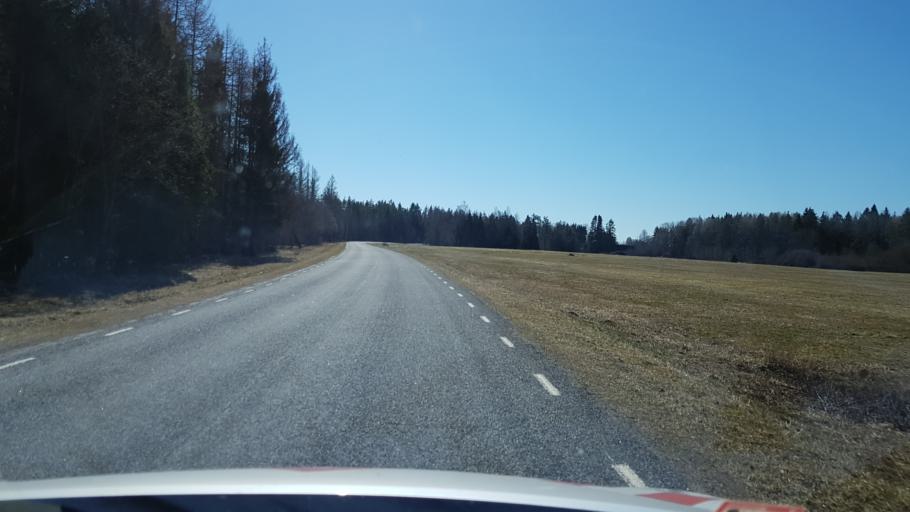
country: EE
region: Laeaene-Virumaa
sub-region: Haljala vald
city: Haljala
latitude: 59.4795
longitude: 26.2478
